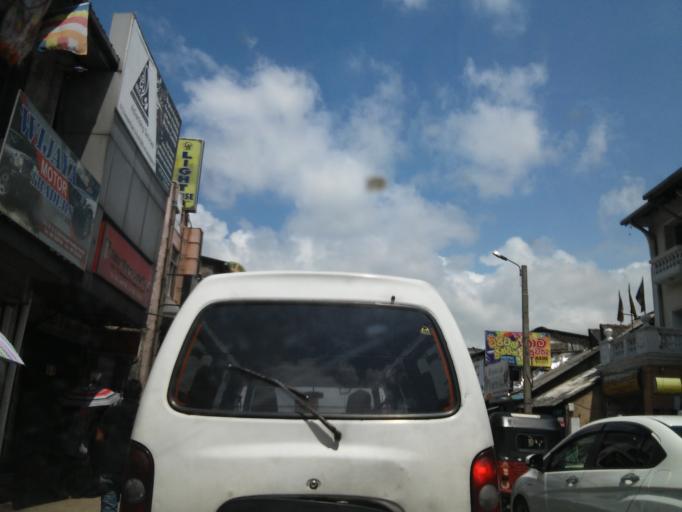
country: LK
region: Central
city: Kandy
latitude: 7.2960
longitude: 80.6377
